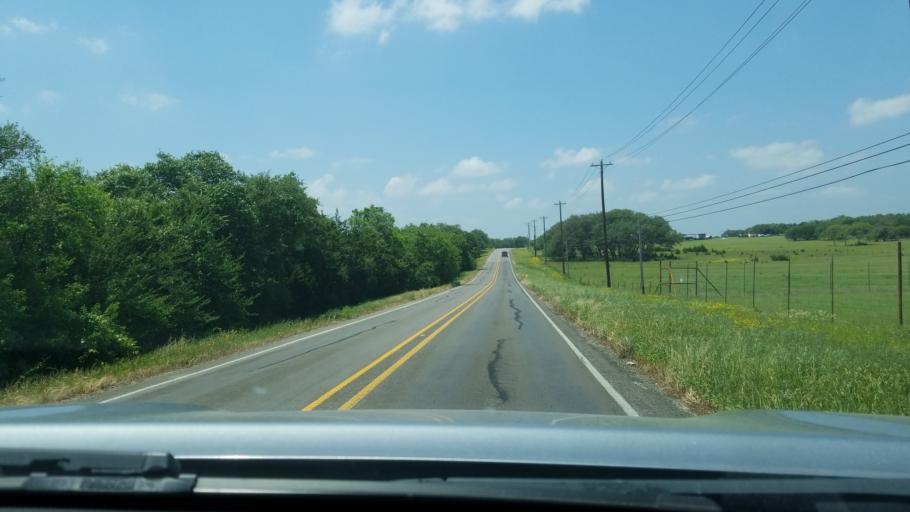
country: US
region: Texas
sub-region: Hays County
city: Woodcreek
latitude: 30.0228
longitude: -98.1583
